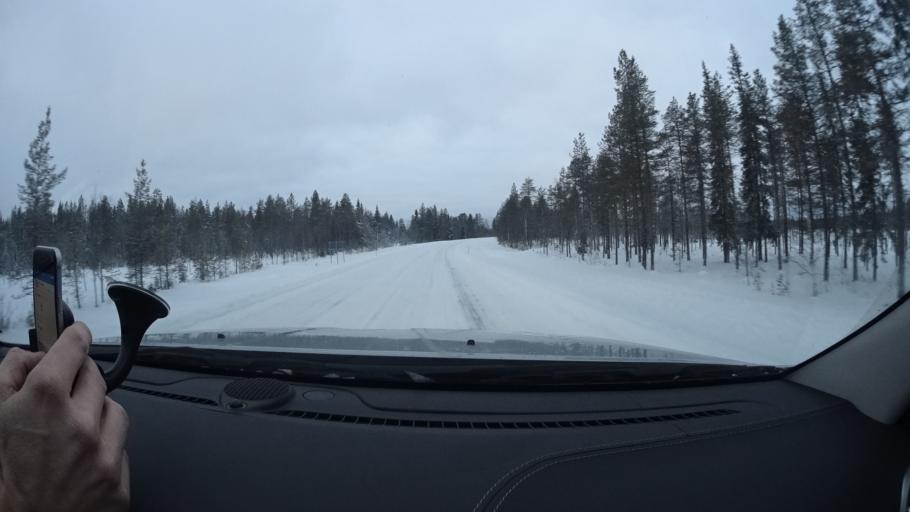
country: FI
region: Lapland
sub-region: Itae-Lappi
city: Posio
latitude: 66.1892
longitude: 27.8421
